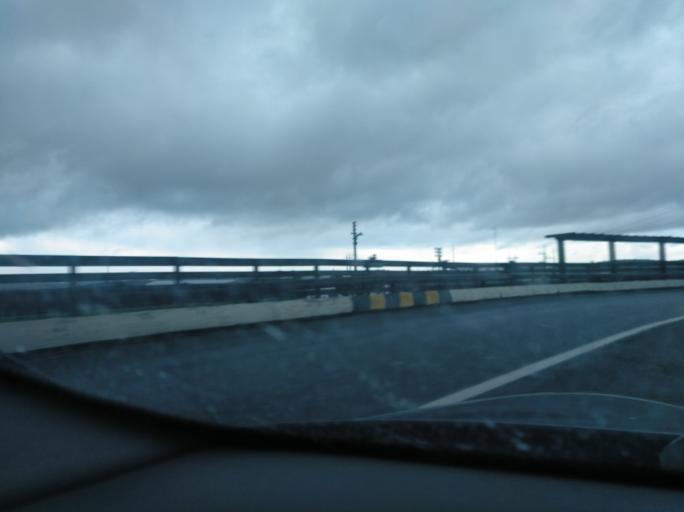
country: PT
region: Beja
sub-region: Aljustrel
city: Aljustrel
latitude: 37.8786
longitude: -8.1544
